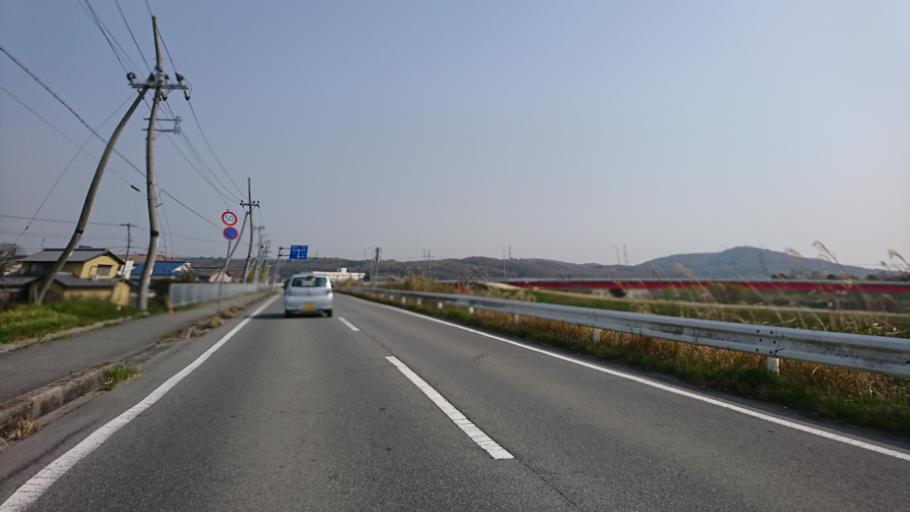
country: JP
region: Hyogo
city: Ono
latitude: 34.8244
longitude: 134.9354
